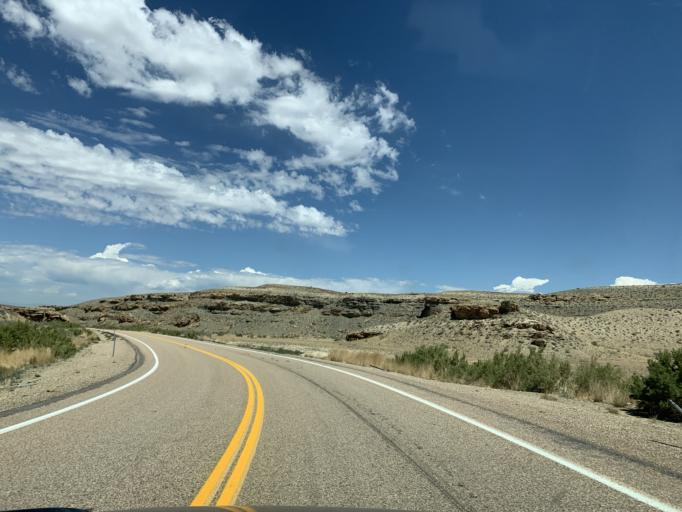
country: US
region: Utah
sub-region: Duchesne County
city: Duchesne
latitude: 40.0117
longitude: -110.1505
